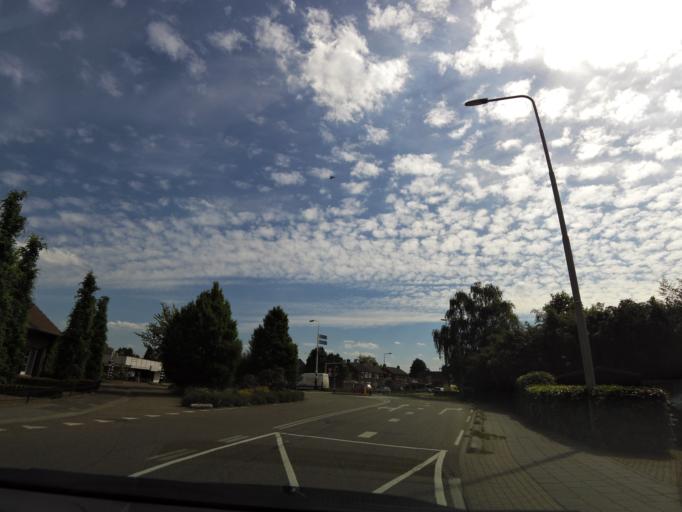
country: NL
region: Limburg
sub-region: Gemeente Leudal
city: Haelen
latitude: 51.2645
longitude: 5.9867
